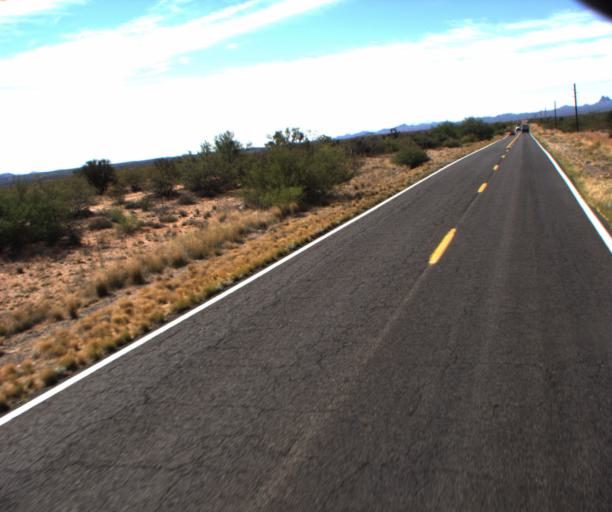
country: US
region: Arizona
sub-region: Yavapai County
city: Congress
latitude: 34.0838
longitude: -112.8254
